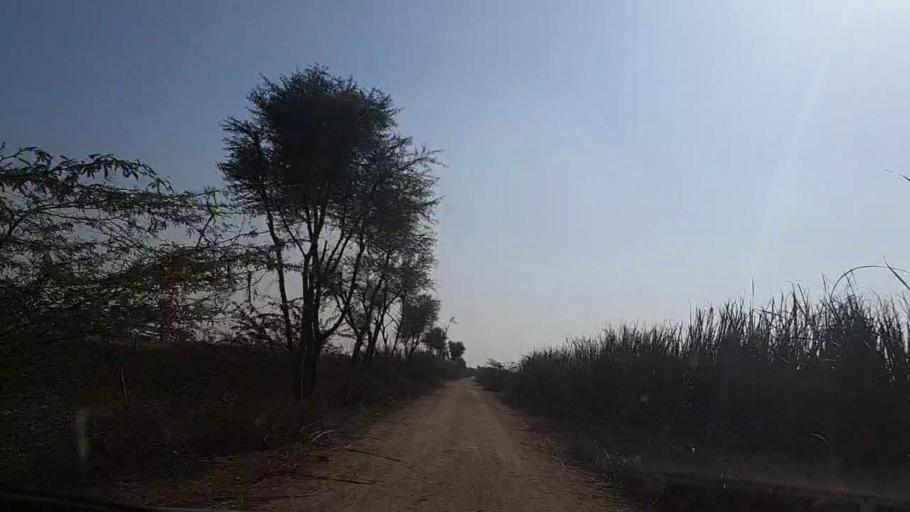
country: PK
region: Sindh
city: Sakrand
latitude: 26.0811
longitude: 68.3694
